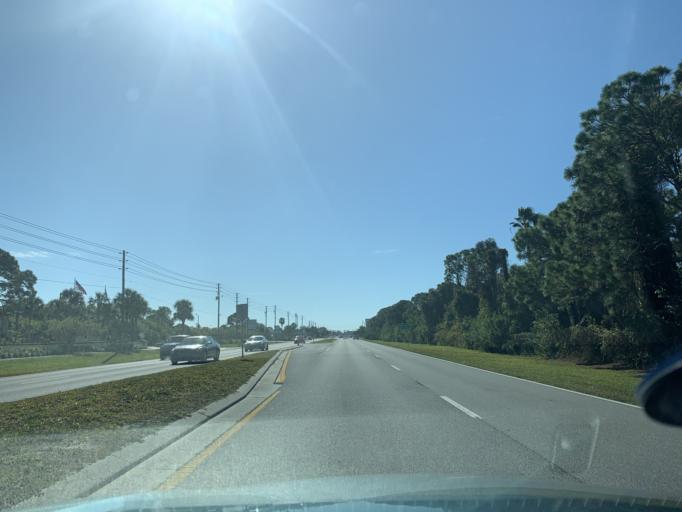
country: US
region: Florida
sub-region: Pinellas County
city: Bay Pines
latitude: 27.8252
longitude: -82.7540
